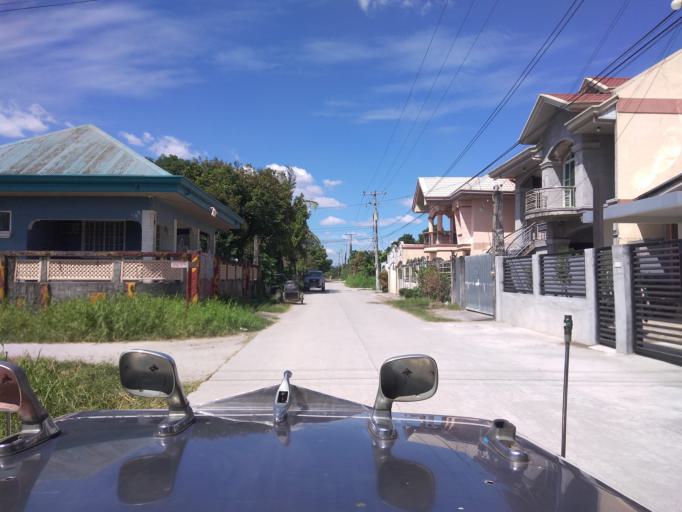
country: PH
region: Central Luzon
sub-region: Province of Pampanga
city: Magliman
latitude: 15.0376
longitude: 120.6509
